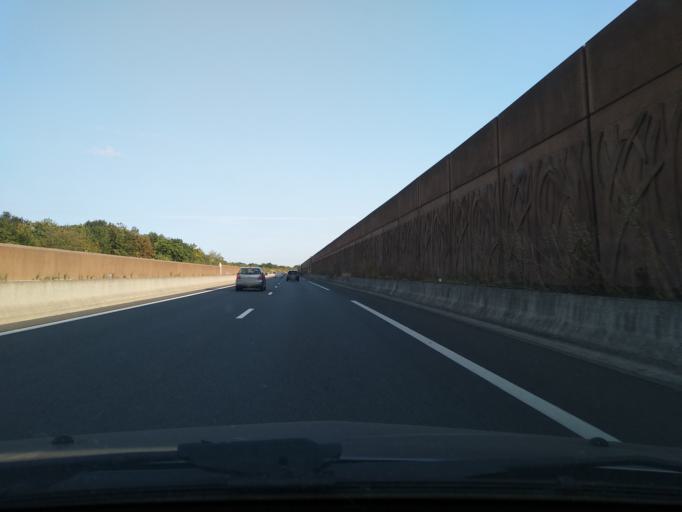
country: FR
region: Centre
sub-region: Departement d'Indre-et-Loire
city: Saint-Cyr-sur-Loire
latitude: 47.4064
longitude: 0.6386
